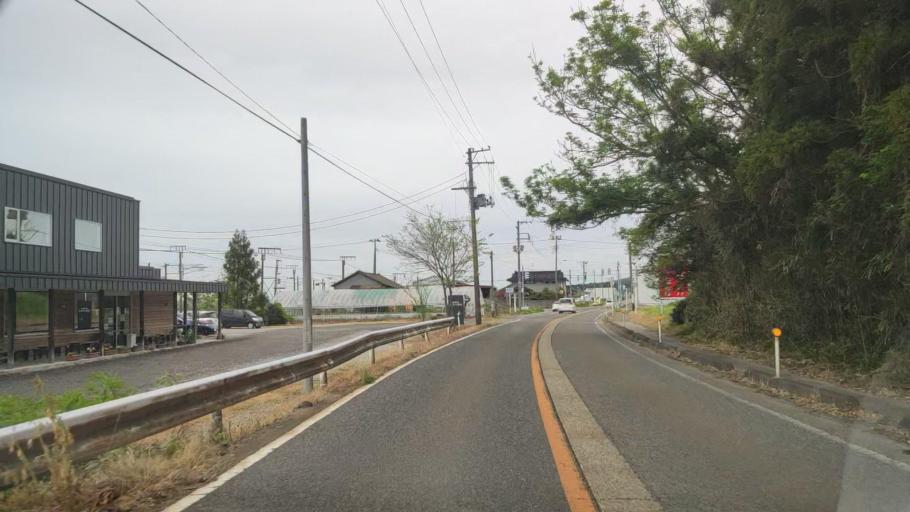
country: JP
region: Niigata
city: Shirone
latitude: 37.7314
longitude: 139.0819
